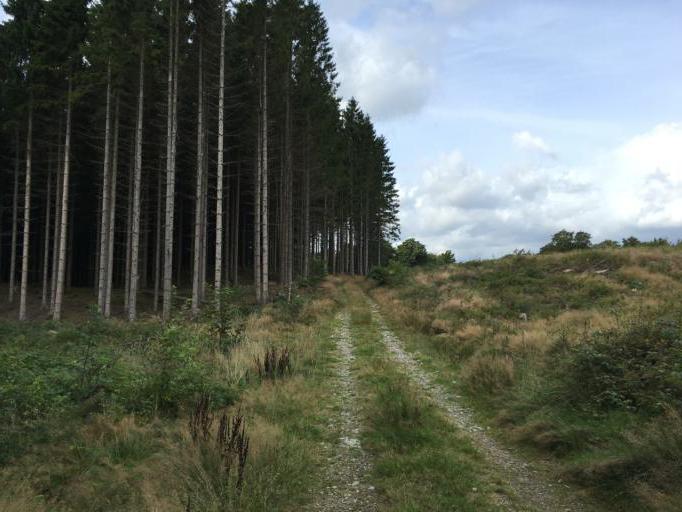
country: SE
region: Skane
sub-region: Hoors Kommun
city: Hoeoer
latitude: 55.9857
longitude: 13.4857
